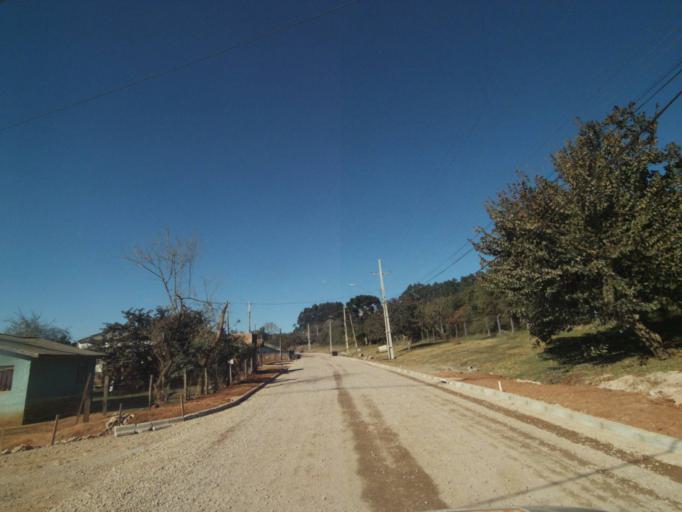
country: BR
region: Parana
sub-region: Tibagi
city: Tibagi
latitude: -24.5212
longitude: -50.4174
